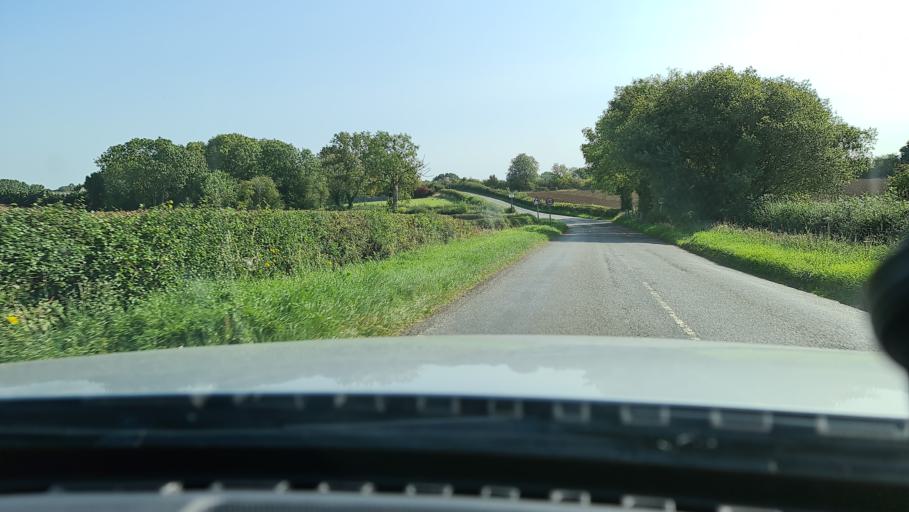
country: GB
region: England
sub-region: Northamptonshire
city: Brackley
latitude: 52.1303
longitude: -1.1809
